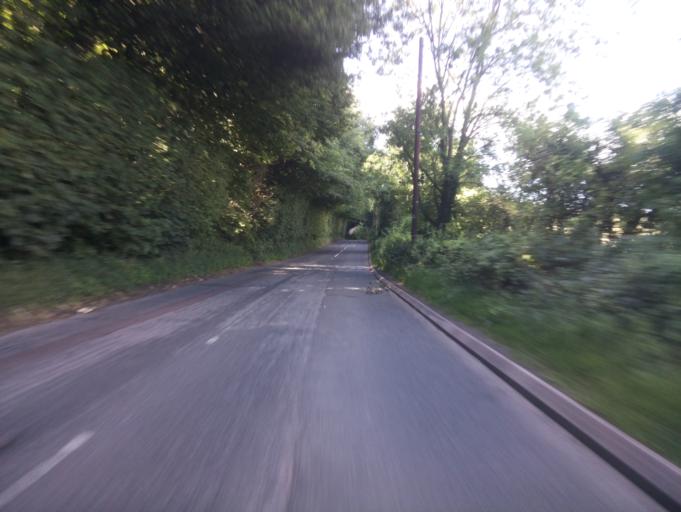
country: GB
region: England
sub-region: Herefordshire
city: Walford
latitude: 51.8735
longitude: -2.6035
